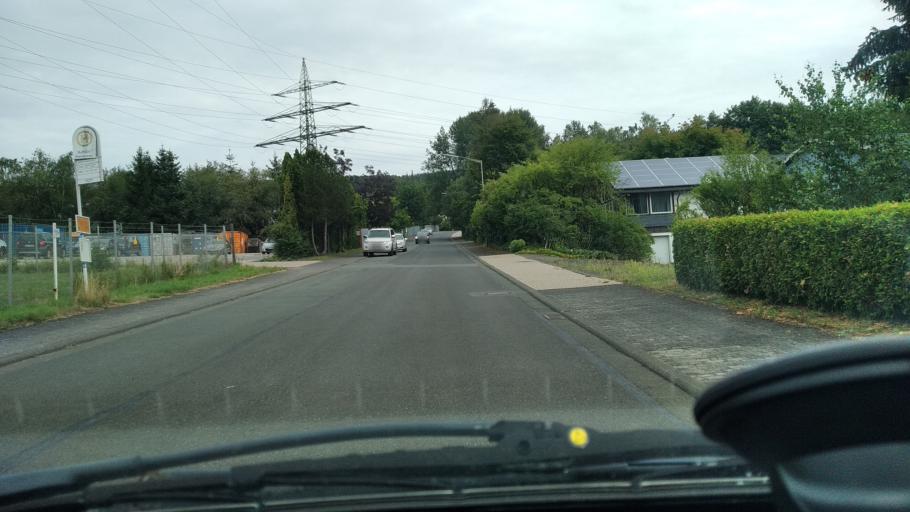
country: DE
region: North Rhine-Westphalia
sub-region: Regierungsbezirk Arnsberg
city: Burbach
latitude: 50.7522
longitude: 8.0995
